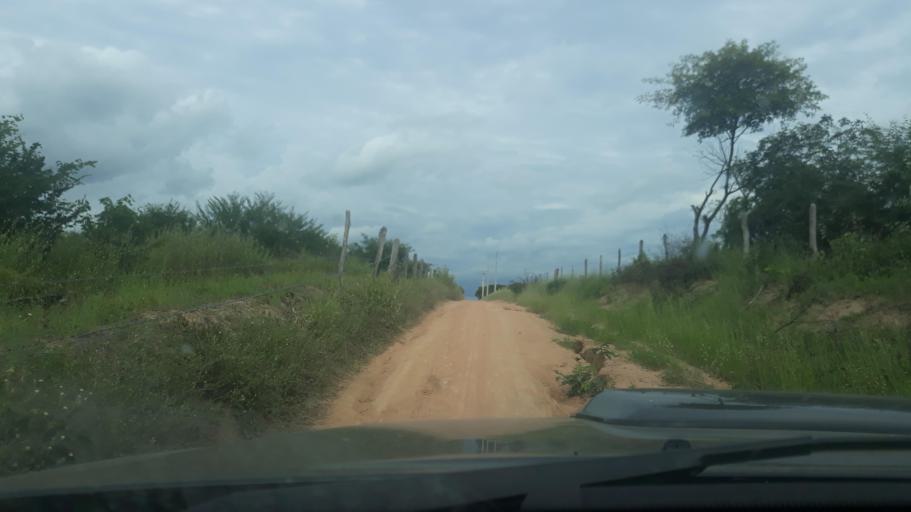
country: BR
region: Bahia
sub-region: Riacho De Santana
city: Riacho de Santana
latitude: -13.8544
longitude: -43.0556
